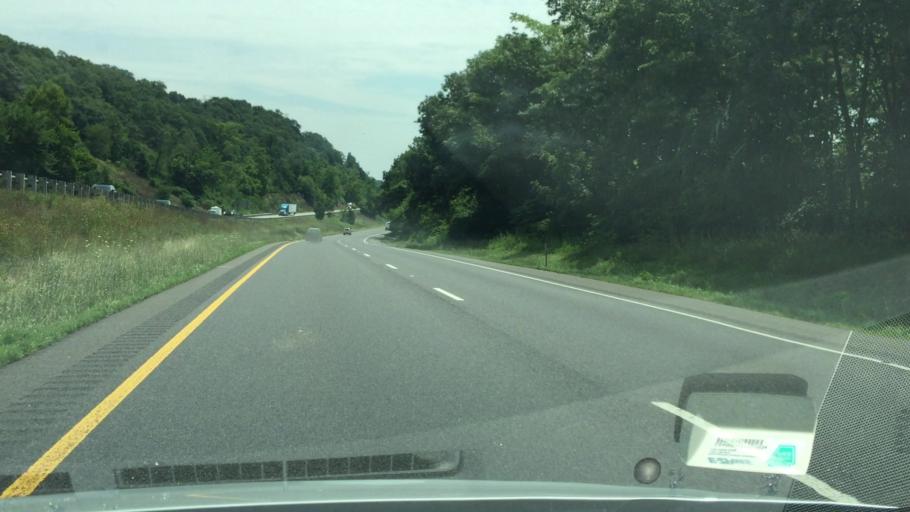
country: US
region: Maryland
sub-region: Washington County
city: Hancock
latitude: 39.6693
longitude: -78.0718
